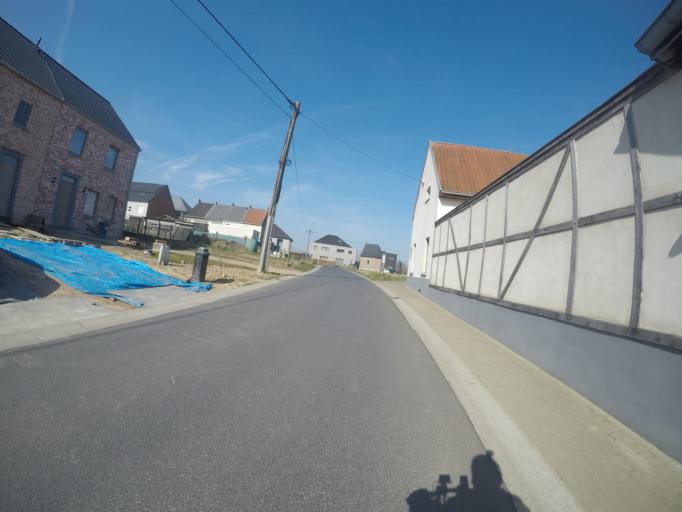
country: BE
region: Flanders
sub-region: Provincie Oost-Vlaanderen
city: Sint-Maria-Lierde
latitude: 50.7824
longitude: 3.8388
